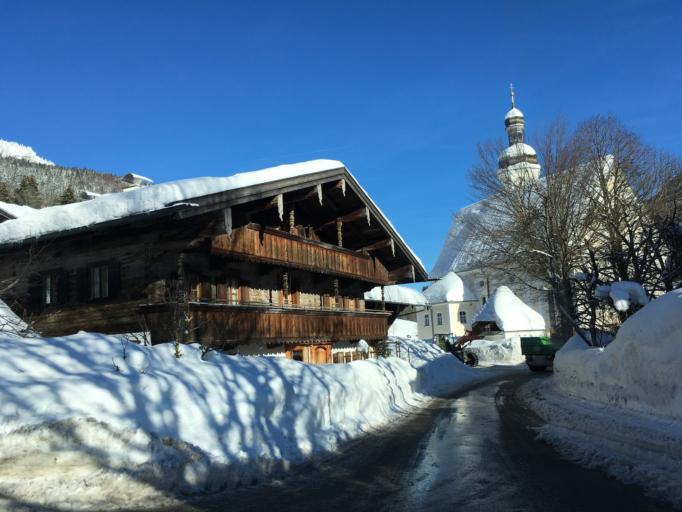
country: AT
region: Tyrol
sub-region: Politischer Bezirk Kufstein
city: Rettenschoss
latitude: 47.6909
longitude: 12.2618
